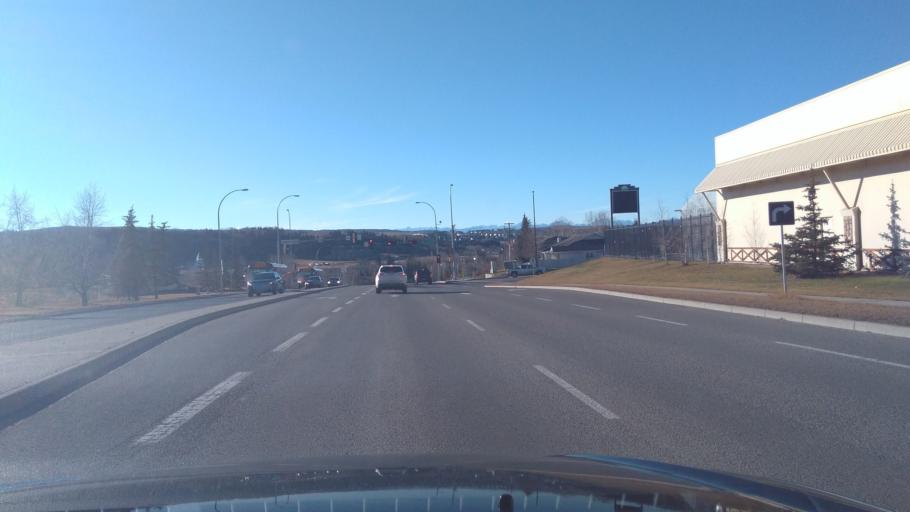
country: CA
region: Alberta
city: Cochrane
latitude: 51.1833
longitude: -114.4767
